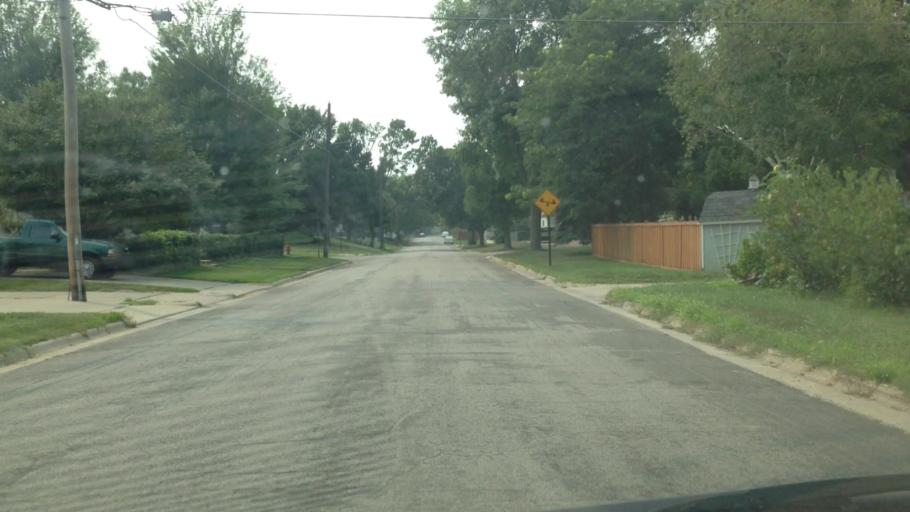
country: US
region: Minnesota
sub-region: Hennepin County
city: Saint Louis Park
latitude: 44.9514
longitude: -93.3660
